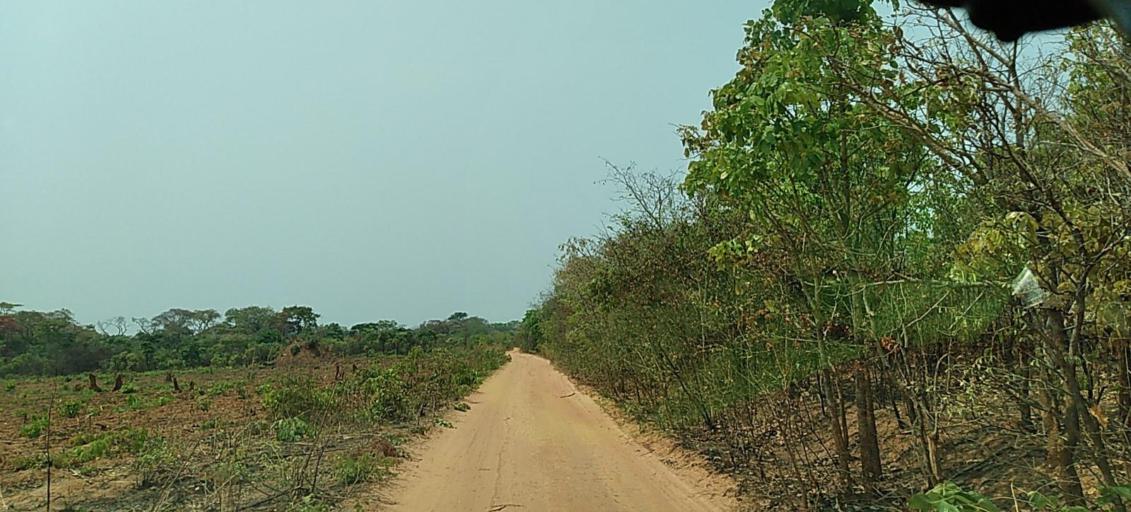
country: ZM
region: North-Western
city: Kabompo
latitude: -13.6967
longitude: 24.3133
